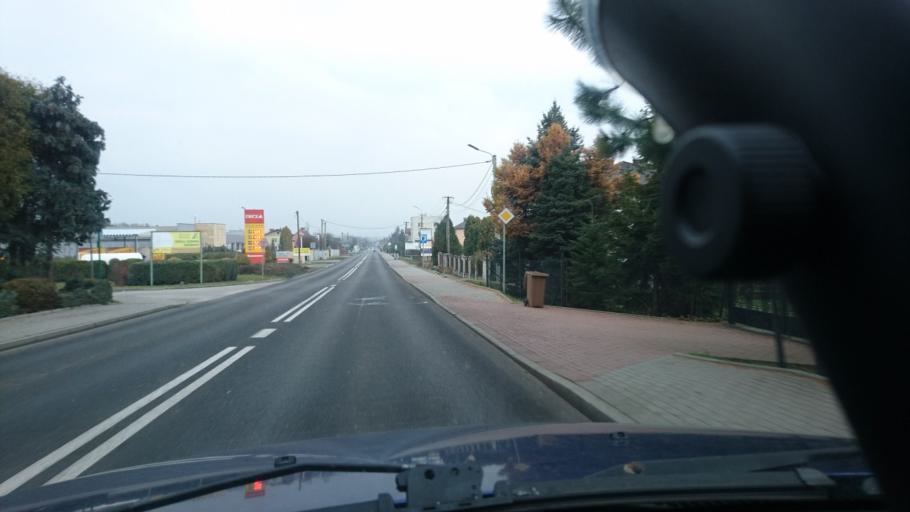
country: PL
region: Silesian Voivodeship
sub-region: Powiat bielski
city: Pisarzowice
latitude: 49.8799
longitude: 19.1377
